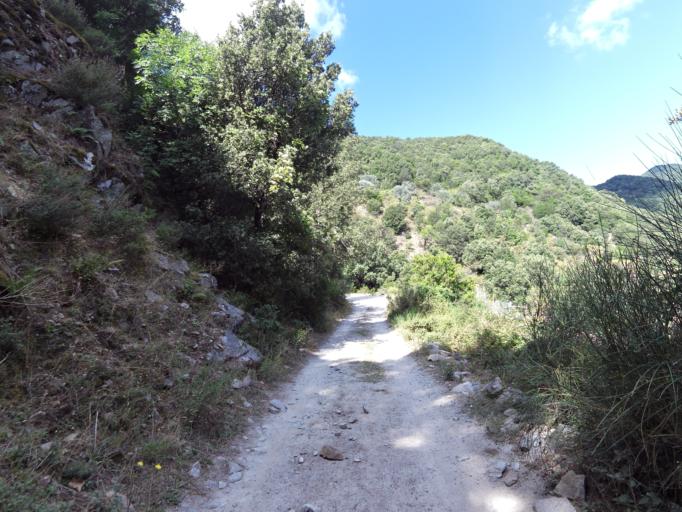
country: IT
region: Calabria
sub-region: Provincia di Reggio Calabria
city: Bivongi
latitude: 38.4890
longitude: 16.4085
